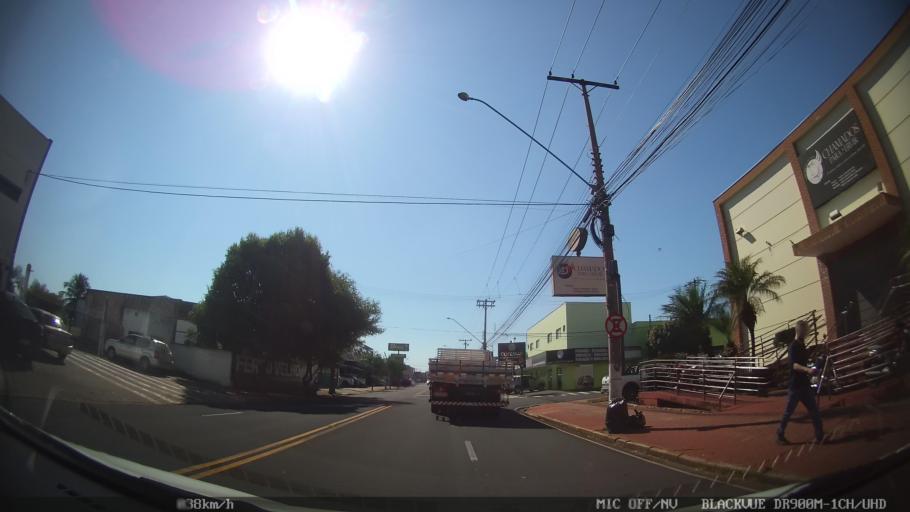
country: BR
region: Sao Paulo
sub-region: Sao Jose Do Rio Preto
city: Sao Jose do Rio Preto
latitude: -20.7971
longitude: -49.3927
